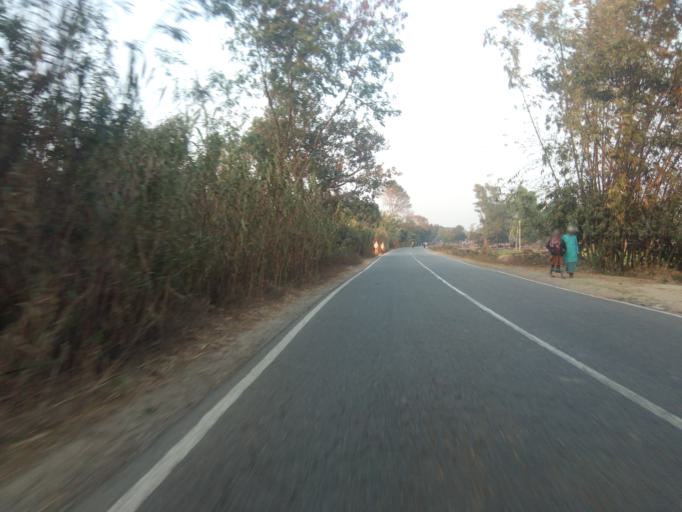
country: BD
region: Rajshahi
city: Bogra
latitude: 24.6237
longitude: 89.2416
